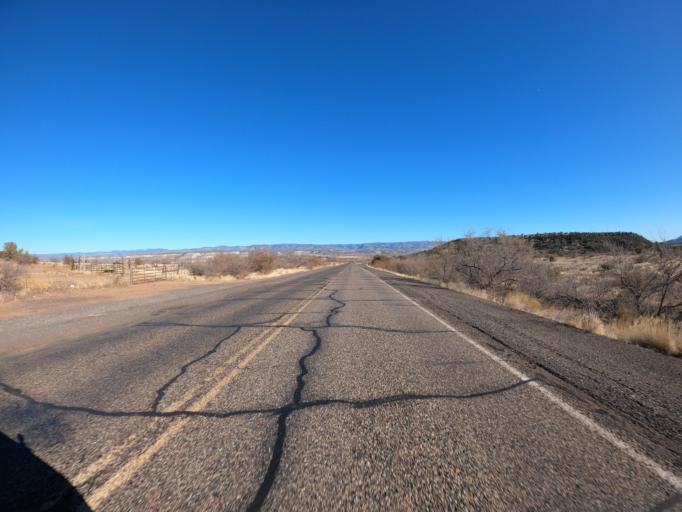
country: US
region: Arizona
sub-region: Yavapai County
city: Camp Verde
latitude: 34.5579
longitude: -111.8912
